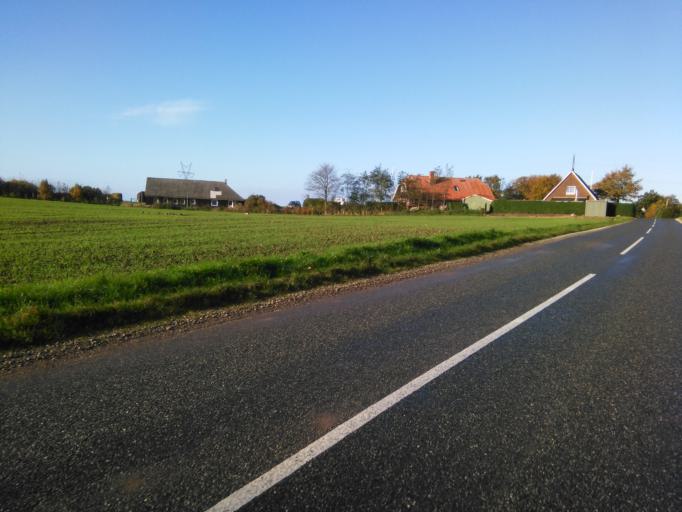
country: DK
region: Central Jutland
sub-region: Arhus Kommune
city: Marslet
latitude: 56.0307
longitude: 10.1413
